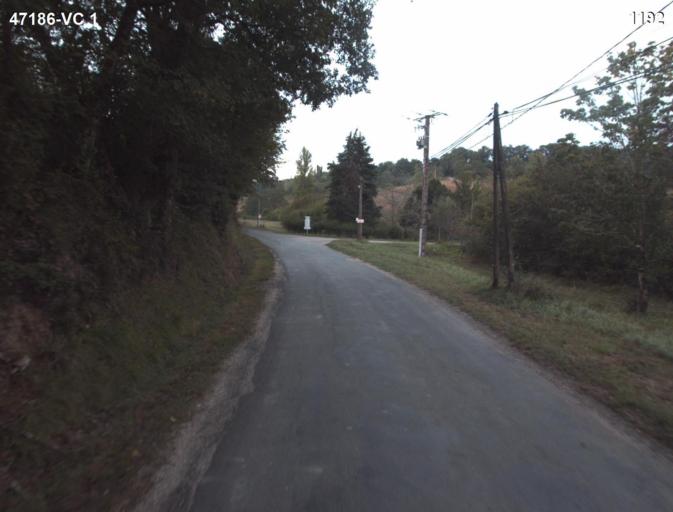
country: FR
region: Aquitaine
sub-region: Departement du Lot-et-Garonne
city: Port-Sainte-Marie
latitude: 44.1978
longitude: 0.4378
